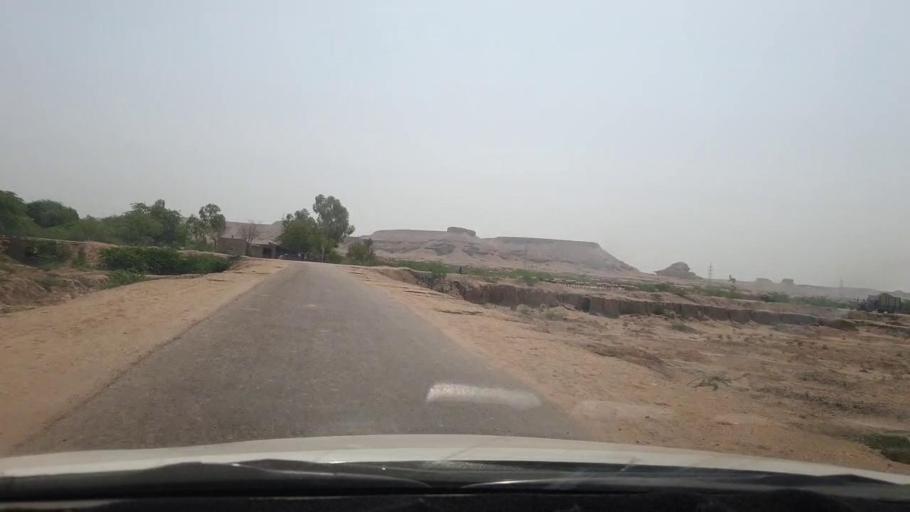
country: PK
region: Sindh
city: Rohri
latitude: 27.6061
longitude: 68.9149
